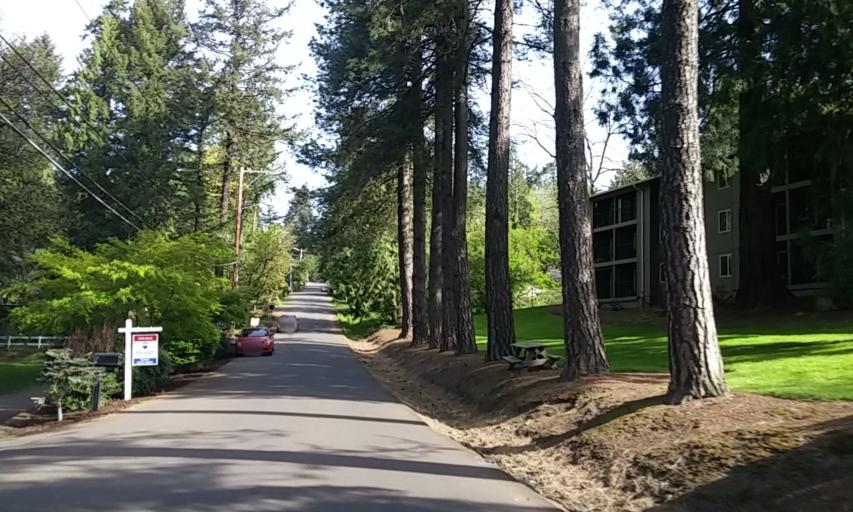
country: US
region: Oregon
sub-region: Washington County
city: West Slope
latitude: 45.5004
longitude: -122.7666
